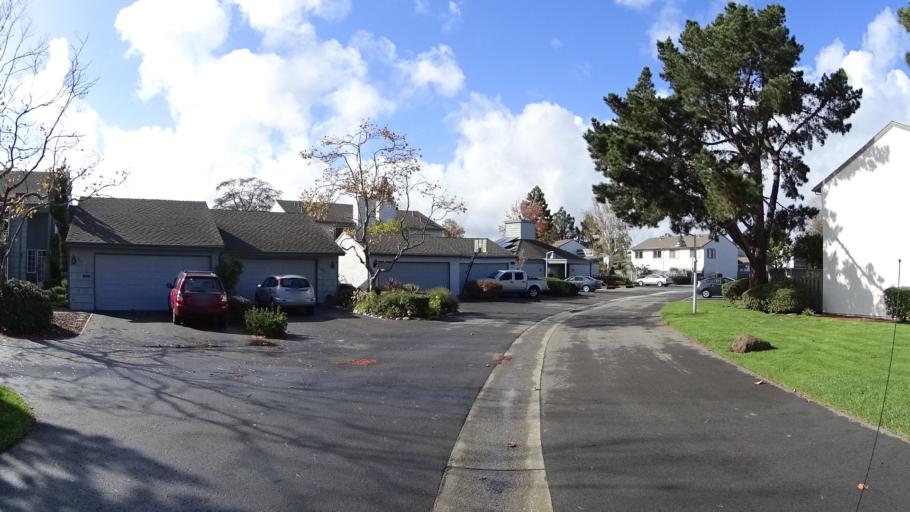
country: US
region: California
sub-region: San Mateo County
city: Foster City
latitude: 37.5509
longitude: -122.2663
